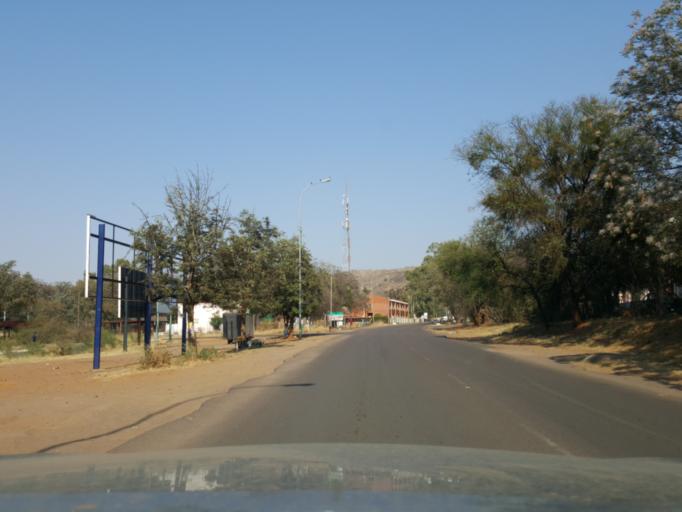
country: BW
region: South East
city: Lobatse
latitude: -25.2285
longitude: 25.6727
